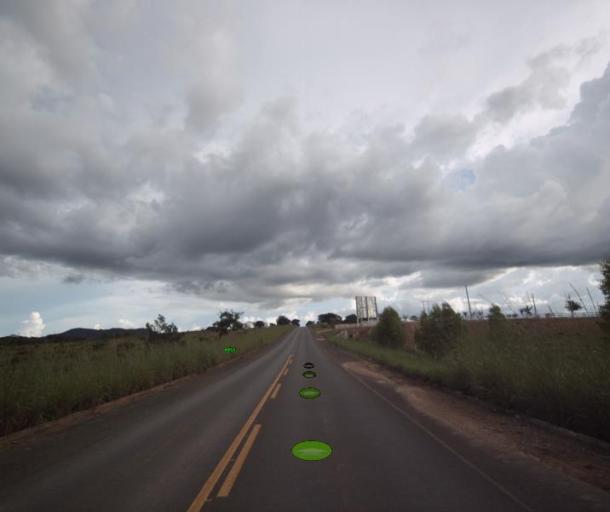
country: BR
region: Goias
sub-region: Niquelandia
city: Niquelandia
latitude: -14.4888
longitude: -48.4894
